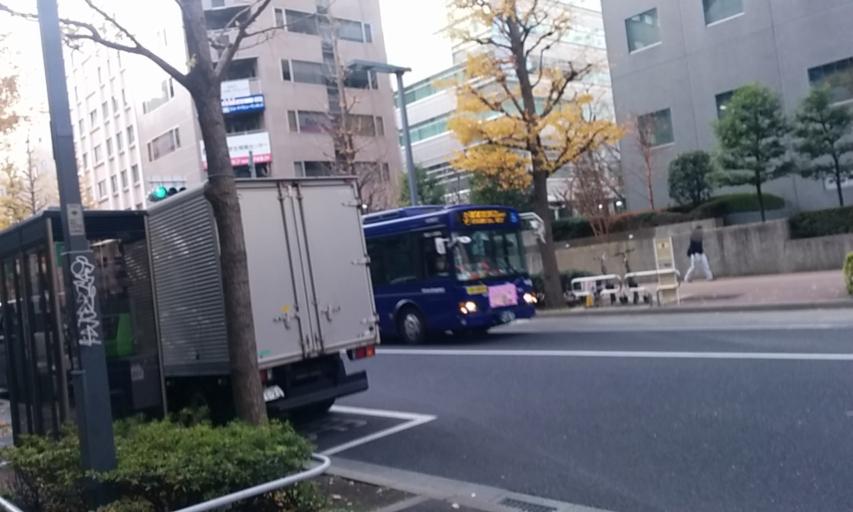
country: JP
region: Tokyo
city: Tokyo
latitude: 35.6904
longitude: 139.6962
